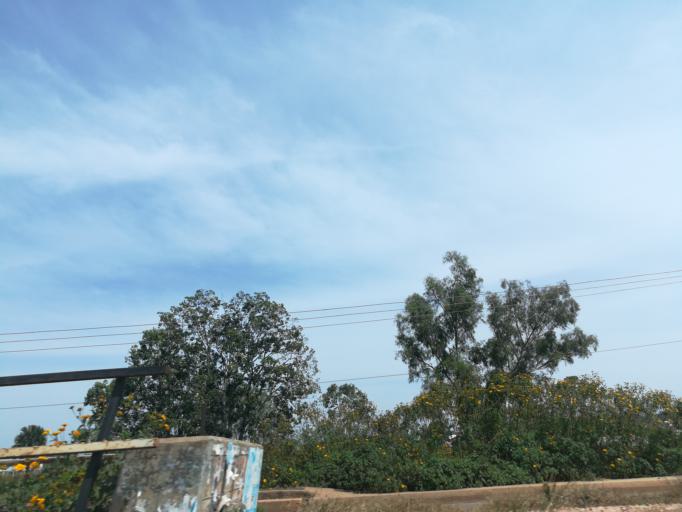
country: NG
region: Plateau
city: Bukuru
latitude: 9.8179
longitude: 8.8656
